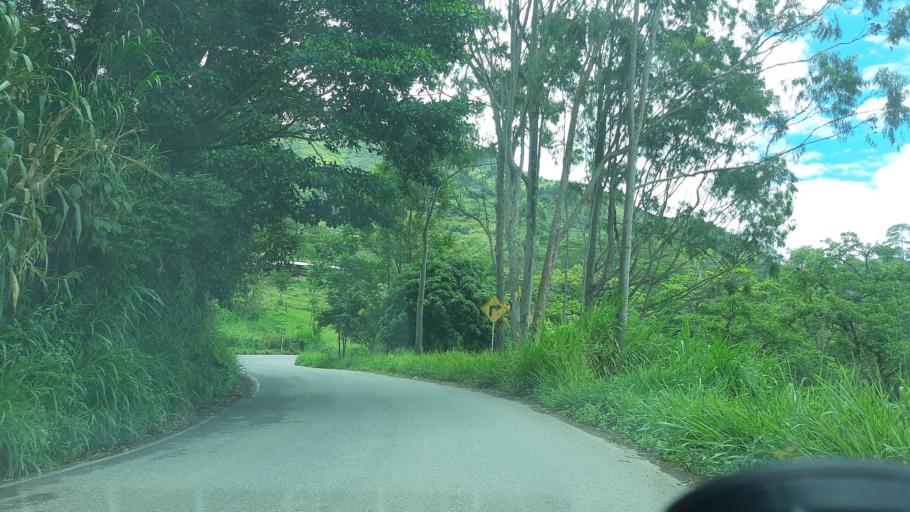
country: CO
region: Boyaca
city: Garagoa
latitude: 5.0407
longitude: -73.3882
